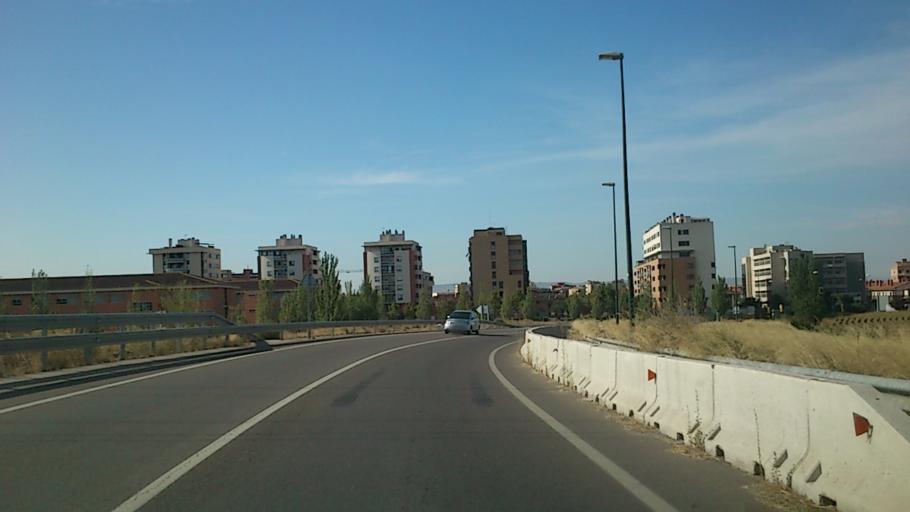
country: ES
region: Aragon
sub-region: Provincia de Zaragoza
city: Zaragoza
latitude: 41.6745
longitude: -0.8300
